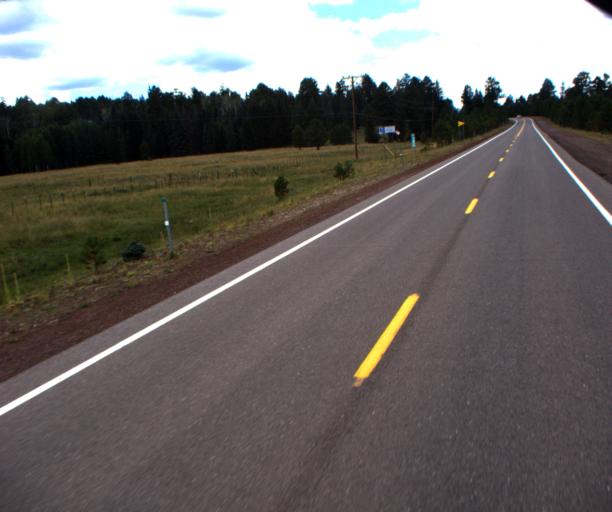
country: US
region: Arizona
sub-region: Apache County
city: Eagar
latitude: 34.0010
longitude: -109.5438
